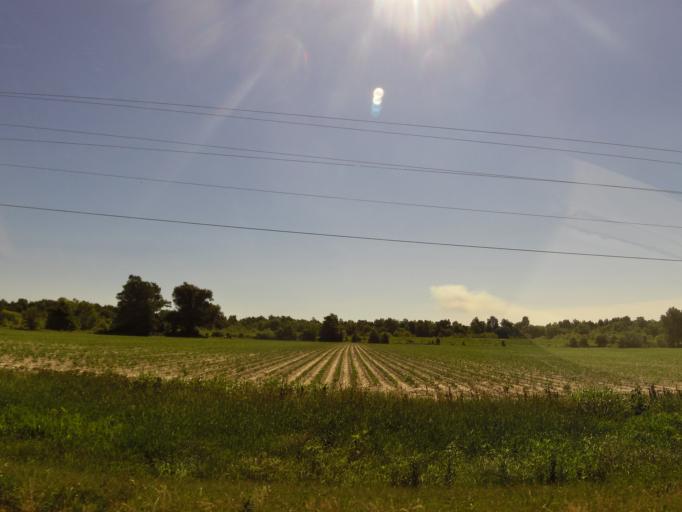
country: US
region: Arkansas
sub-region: Clay County
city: Piggott
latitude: 36.4343
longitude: -90.1473
